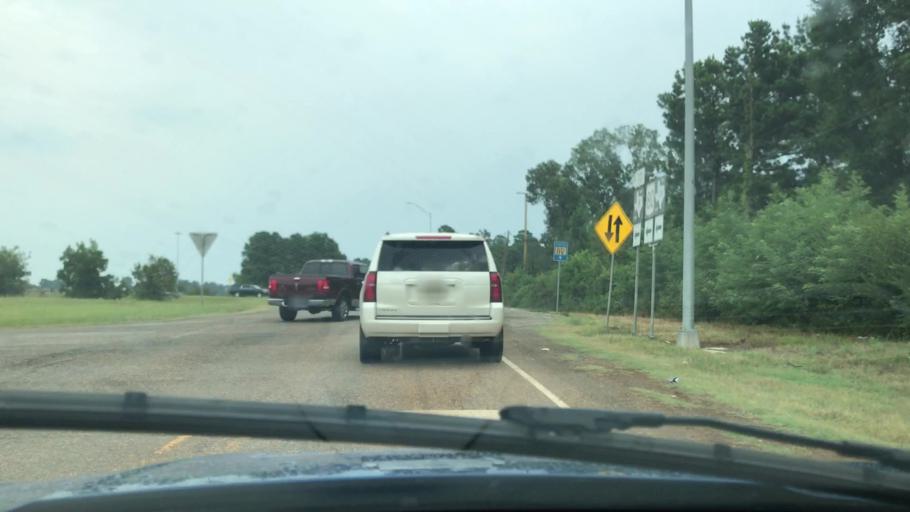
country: US
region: Texas
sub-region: Harrison County
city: Waskom
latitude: 32.4783
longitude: -94.0890
